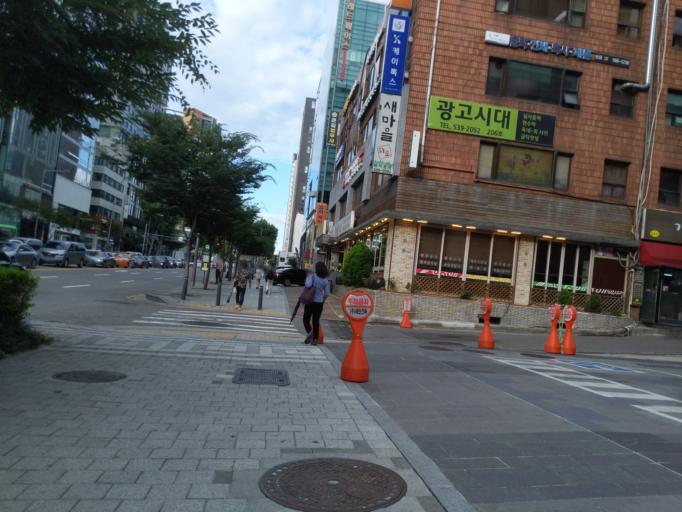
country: KR
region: Seoul
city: Seoul
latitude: 37.5076
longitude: 127.0348
